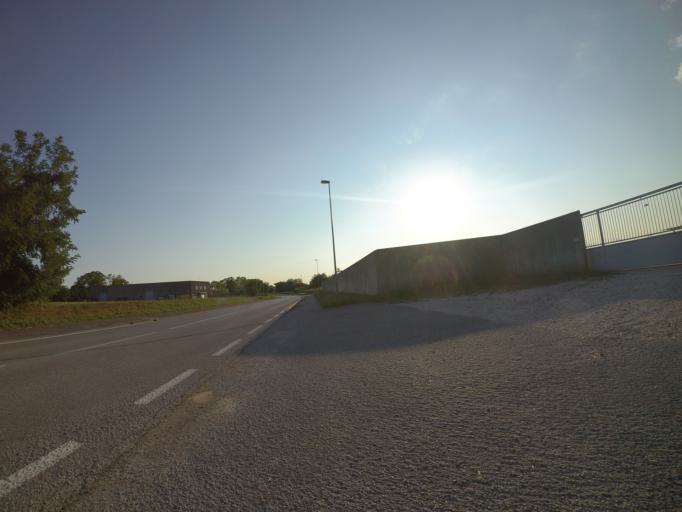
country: IT
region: Friuli Venezia Giulia
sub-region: Provincia di Udine
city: Pasian di Prato
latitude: 46.0413
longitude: 13.1797
